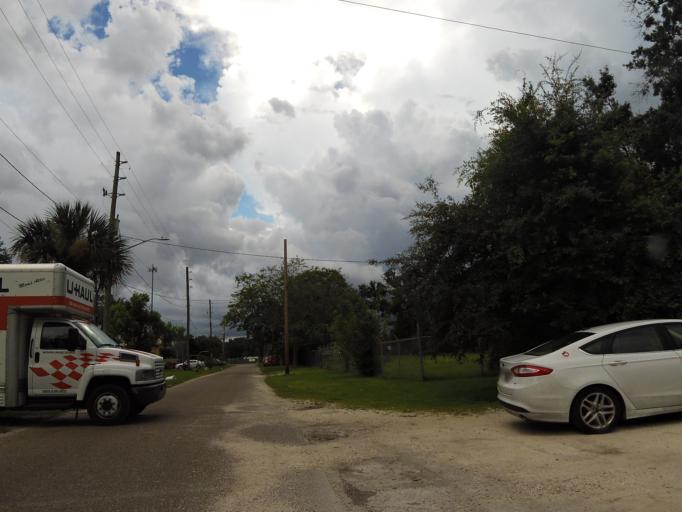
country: US
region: Florida
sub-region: Duval County
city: Jacksonville
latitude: 30.3465
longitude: -81.6439
